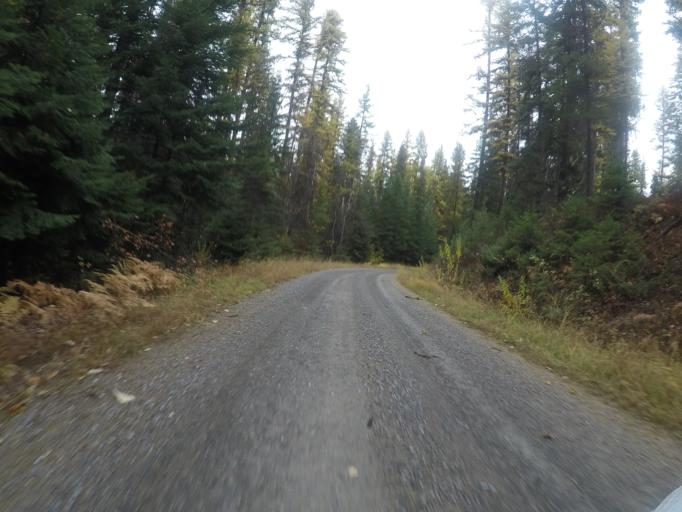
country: US
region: Montana
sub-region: Flathead County
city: Bigfork
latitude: 47.8860
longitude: -113.8650
